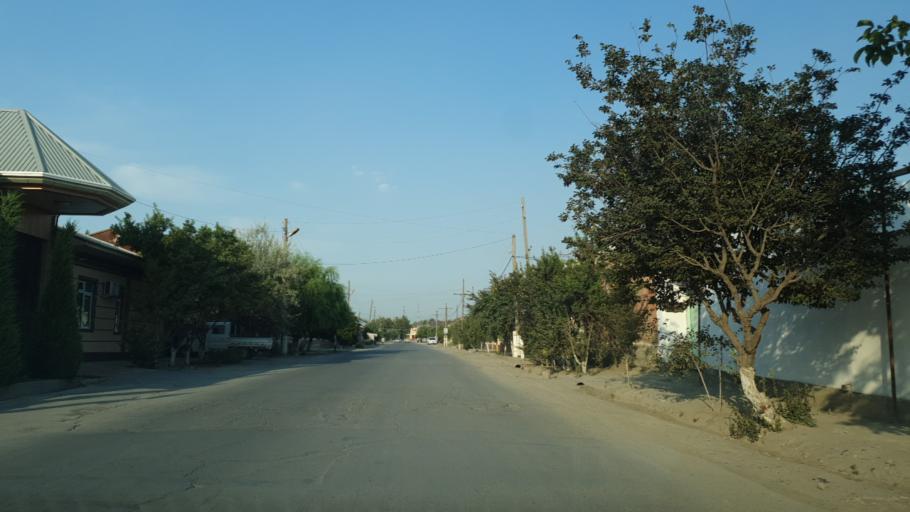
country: UZ
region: Fergana
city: Yaypan
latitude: 40.3784
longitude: 70.8009
